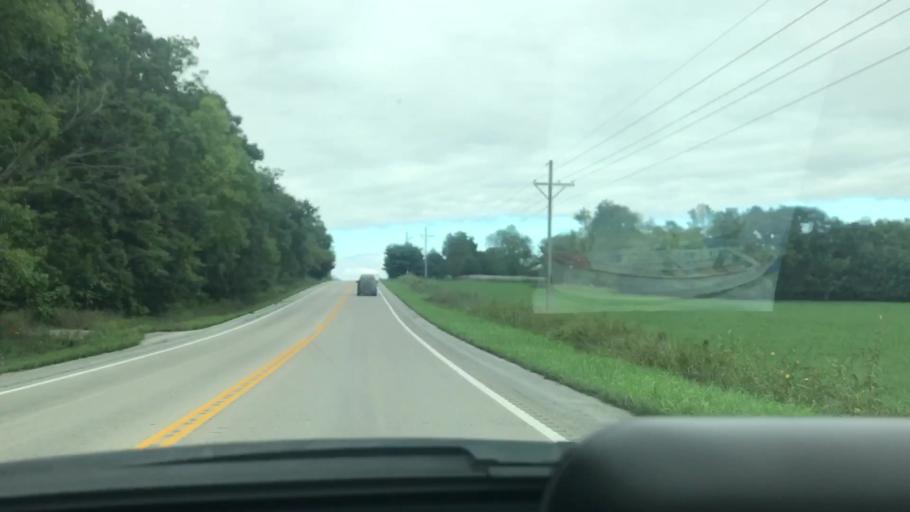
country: US
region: Missouri
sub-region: Hickory County
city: Hermitage
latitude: 37.8772
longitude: -93.1804
